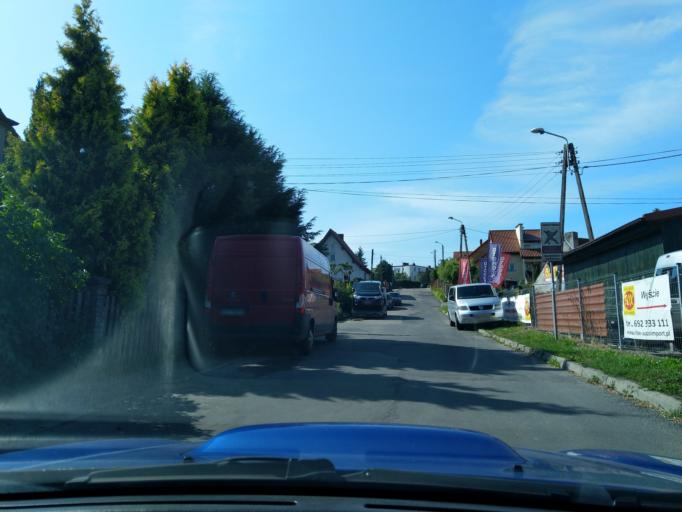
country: PL
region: Warmian-Masurian Voivodeship
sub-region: Olsztyn
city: Kortowo
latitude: 53.7702
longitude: 20.4401
